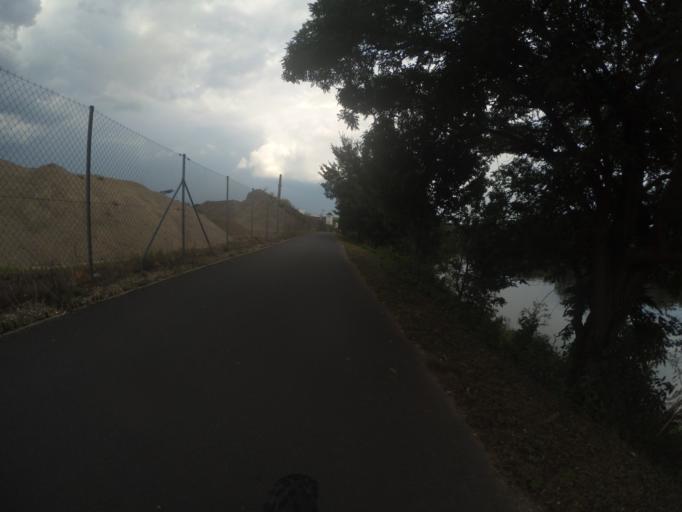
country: CZ
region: Central Bohemia
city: Dolni Berkovice
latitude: 50.3817
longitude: 14.4518
